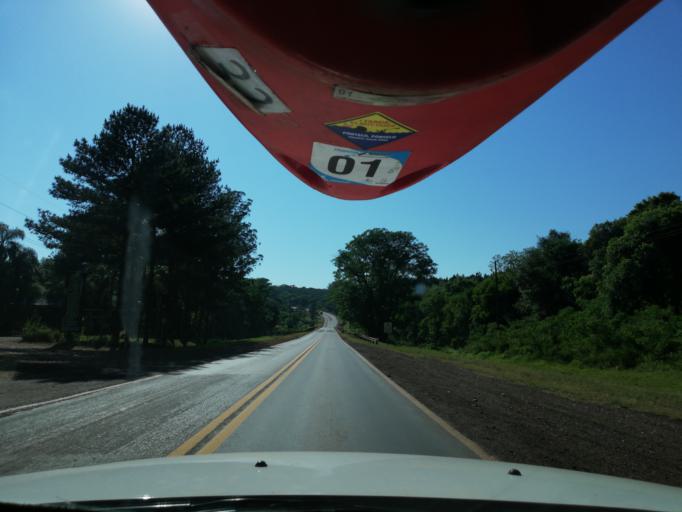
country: AR
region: Misiones
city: Puerto Leoni
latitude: -27.0100
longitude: -55.1768
